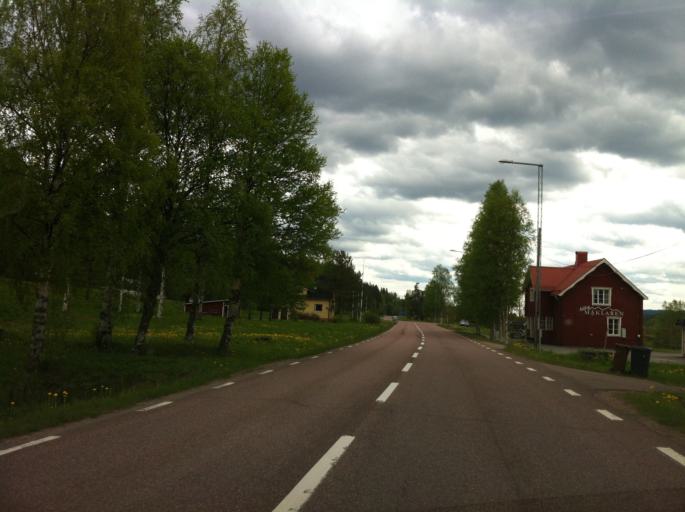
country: SE
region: Dalarna
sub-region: Malung-Saelens kommun
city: Malung
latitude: 61.1904
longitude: 13.2393
